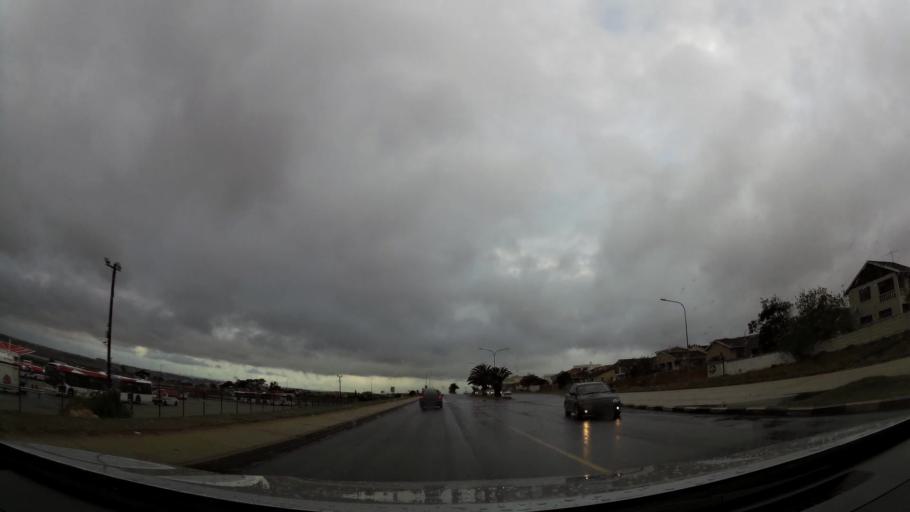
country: ZA
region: Eastern Cape
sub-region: Nelson Mandela Bay Metropolitan Municipality
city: Port Elizabeth
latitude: -33.8911
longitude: 25.5222
